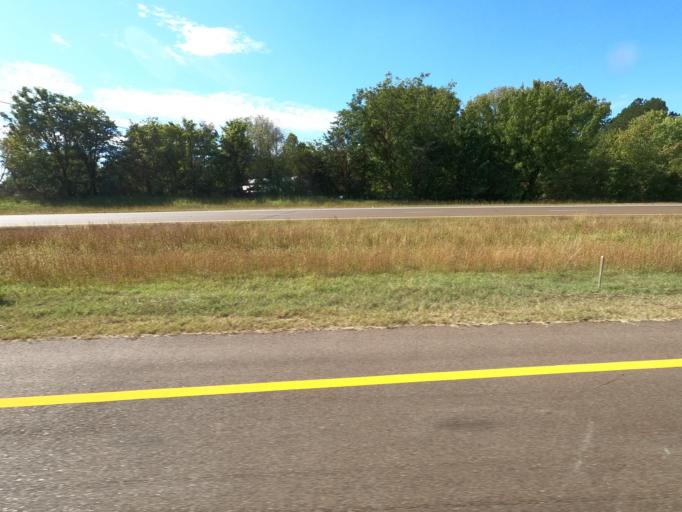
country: US
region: Tennessee
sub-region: Dyer County
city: Dyersburg
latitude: 35.9758
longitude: -89.3399
